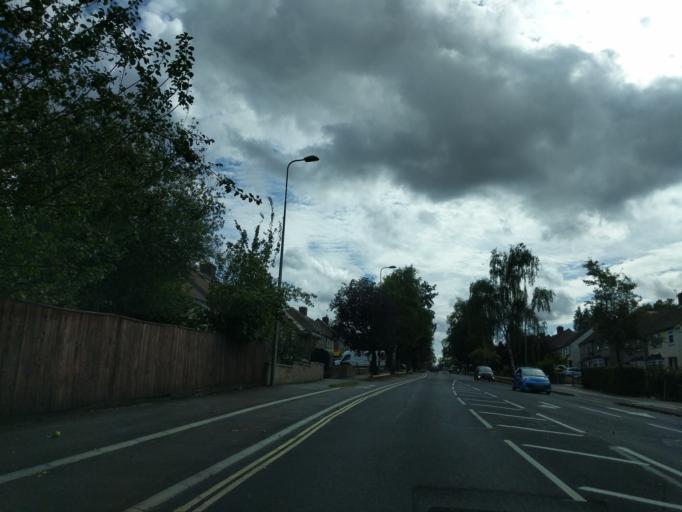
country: GB
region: England
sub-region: Oxfordshire
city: Oxford
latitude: 51.7630
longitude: -1.2247
